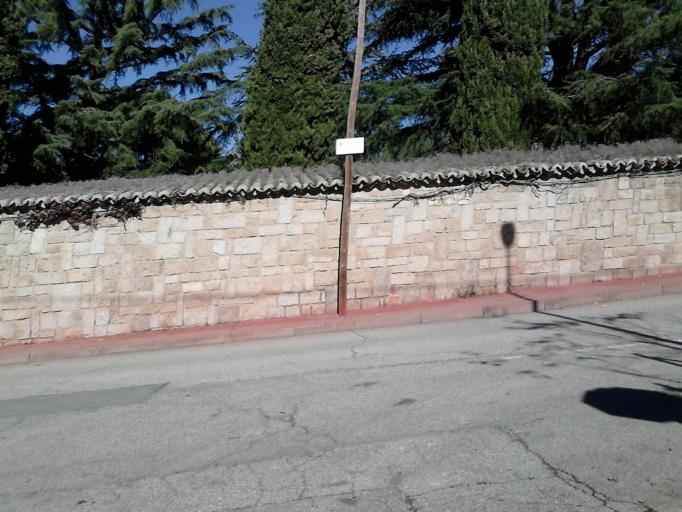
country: ES
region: Madrid
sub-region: Provincia de Madrid
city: Galapagar
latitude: 40.5739
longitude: -3.9955
